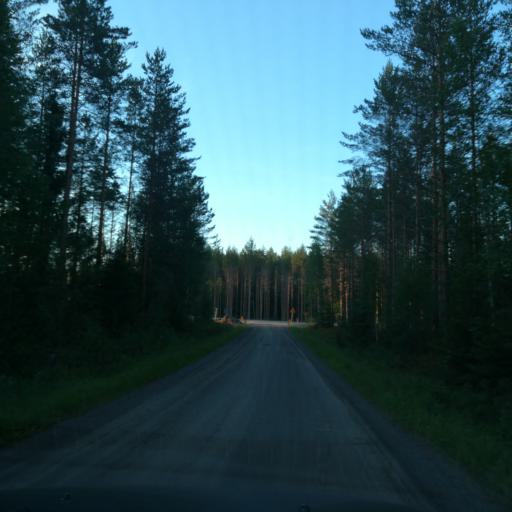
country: FI
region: Southern Savonia
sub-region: Mikkeli
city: Puumala
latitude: 61.4366
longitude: 28.4753
